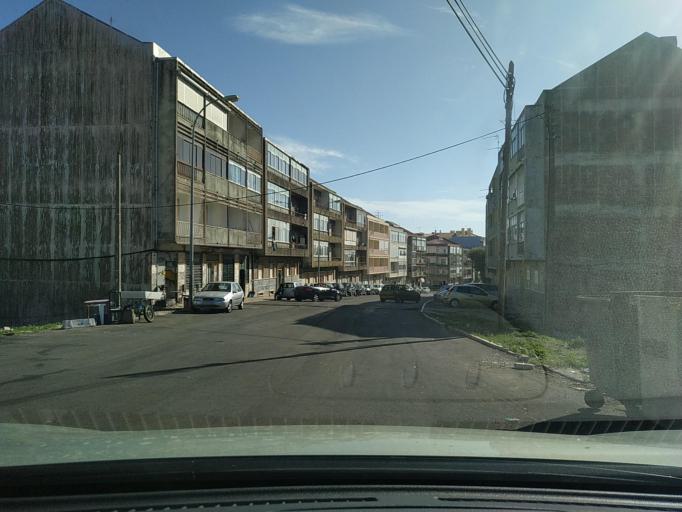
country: PT
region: Lisbon
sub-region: Amadora
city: Amadora
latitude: 38.7642
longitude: -9.2410
